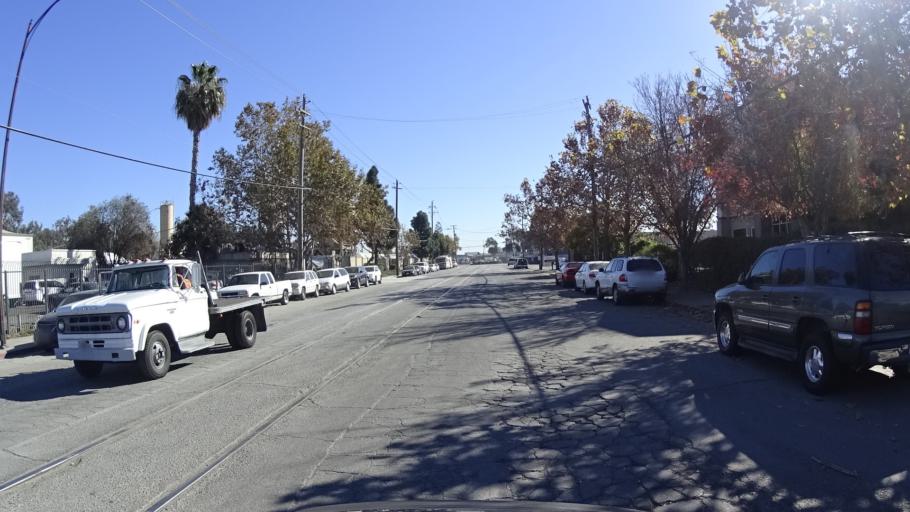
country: US
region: California
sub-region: Santa Clara County
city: San Jose
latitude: 37.3711
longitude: -121.9055
